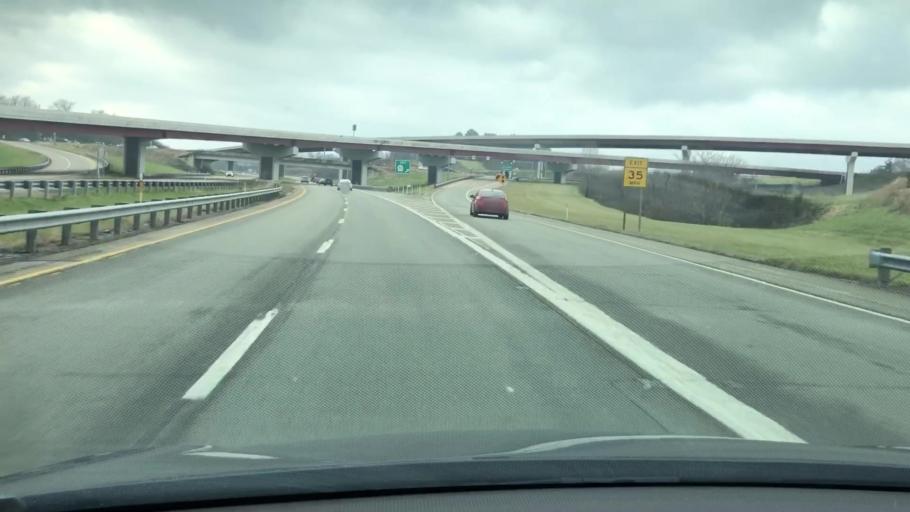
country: US
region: Pennsylvania
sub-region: Fayette County
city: Oliver
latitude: 39.9178
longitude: -79.7238
